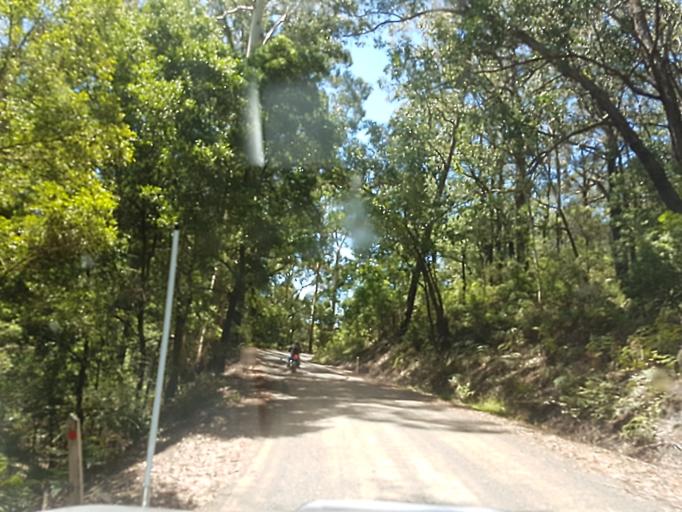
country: AU
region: Victoria
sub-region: Colac-Otway
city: Apollo Bay
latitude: -38.6396
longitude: 143.3102
